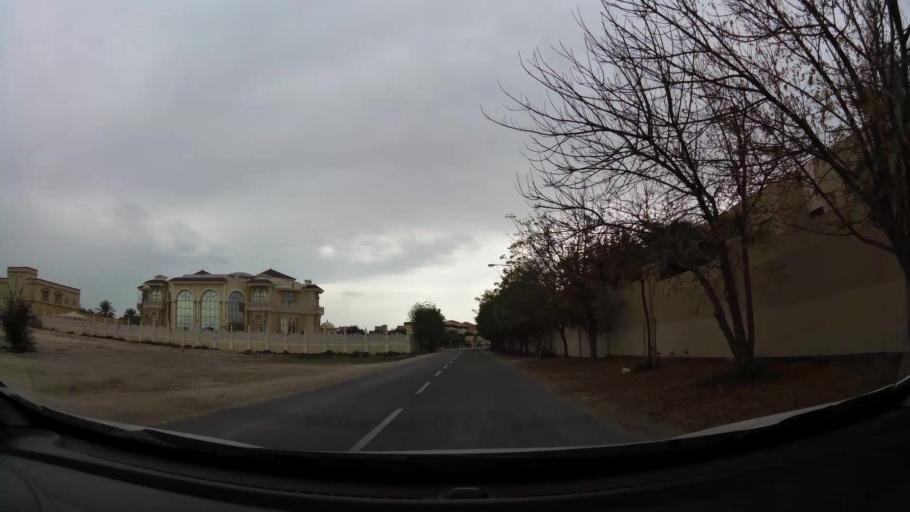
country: BH
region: Central Governorate
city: Madinat Hamad
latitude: 26.1502
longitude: 50.4714
